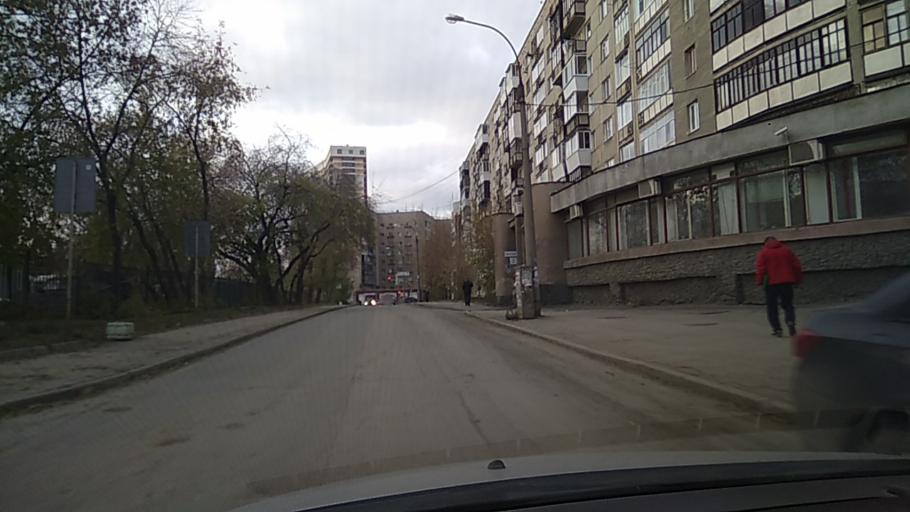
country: RU
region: Sverdlovsk
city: Yekaterinburg
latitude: 56.8525
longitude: 60.5840
